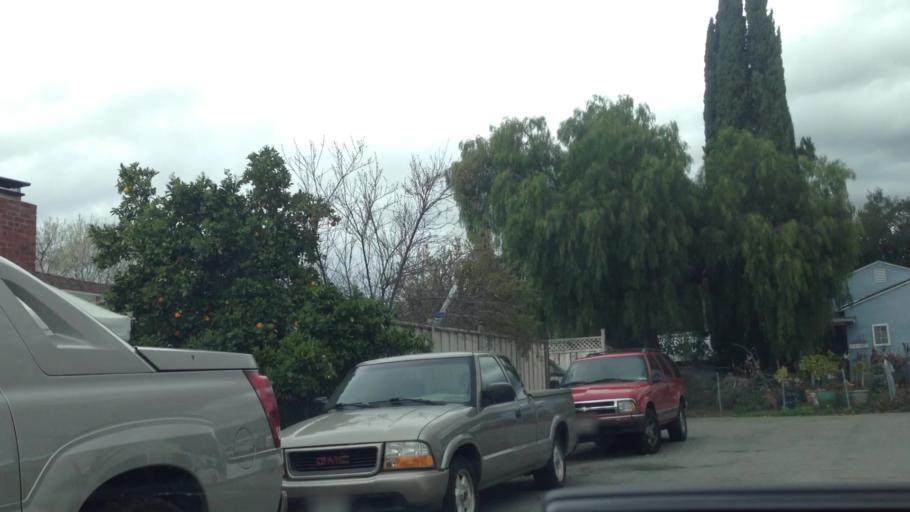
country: US
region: California
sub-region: Santa Clara County
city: Alum Rock
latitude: 37.3675
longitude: -121.8235
